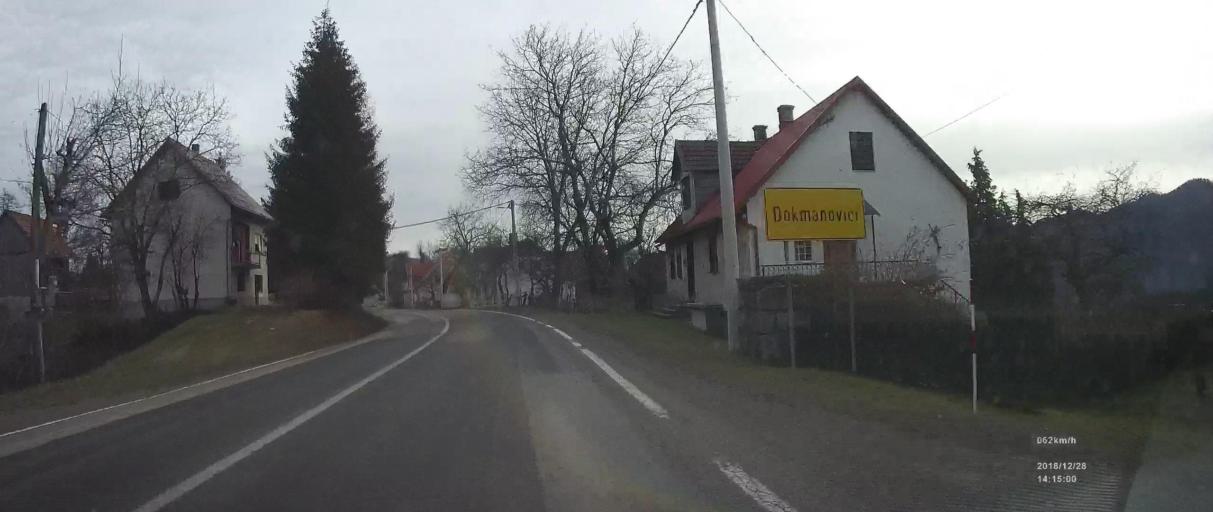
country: HR
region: Primorsko-Goranska
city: Vrbovsko
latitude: 45.4276
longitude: 15.0242
